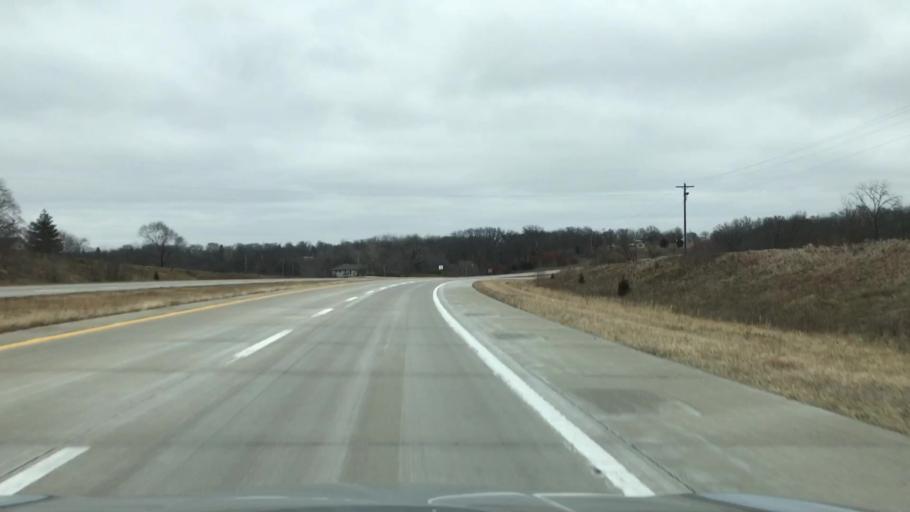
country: US
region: Missouri
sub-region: Livingston County
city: Chillicothe
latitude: 39.7400
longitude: -93.6431
